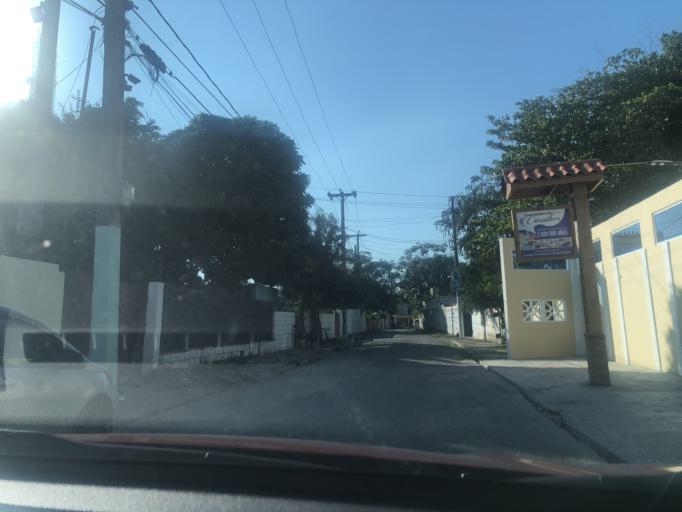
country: DO
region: Santo Domingo
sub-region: Santo Domingo
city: Boca Chica
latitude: 18.4539
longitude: -69.6100
